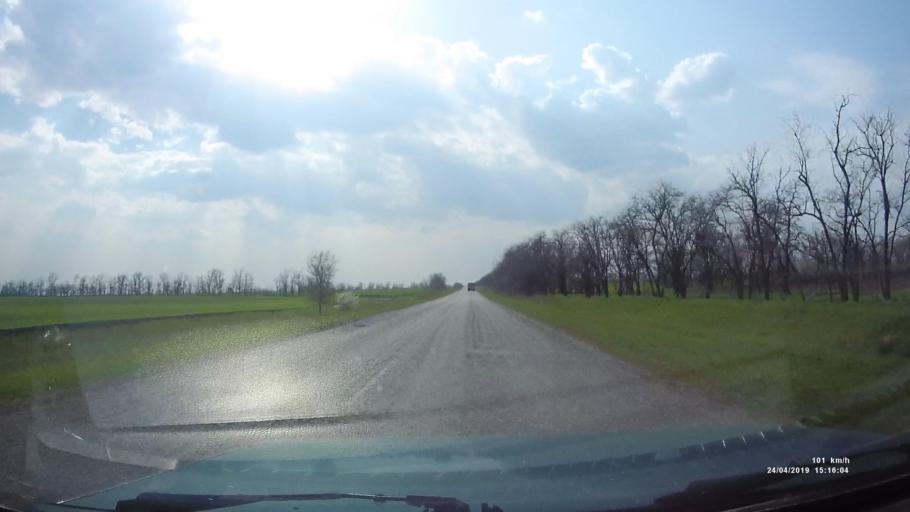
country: RU
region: Rostov
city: Remontnoye
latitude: 46.5473
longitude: 43.2216
